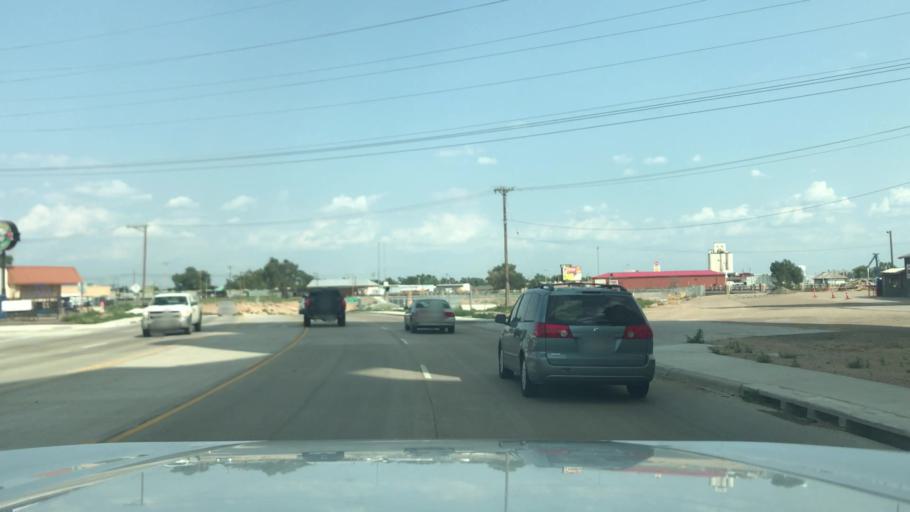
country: US
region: Texas
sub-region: Dallam County
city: Dalhart
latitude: 36.0674
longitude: -102.5247
